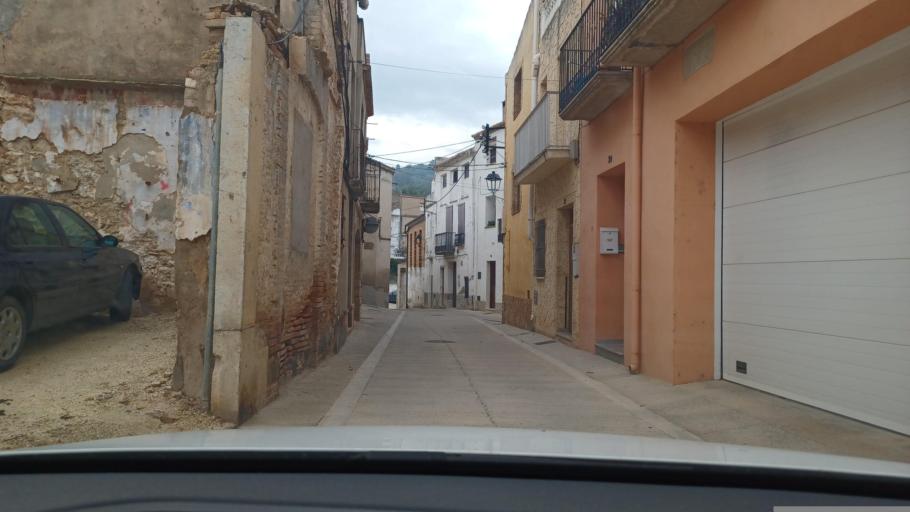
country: ES
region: Catalonia
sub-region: Provincia de Tarragona
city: Ulldecona
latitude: 40.6550
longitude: 0.4706
